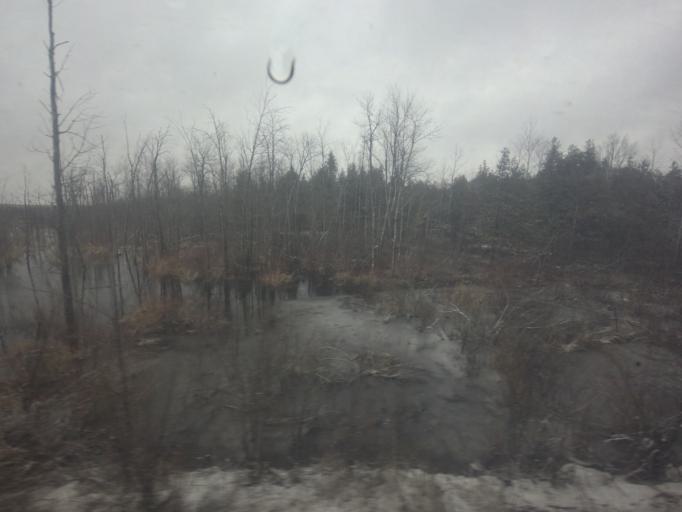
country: CA
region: Ontario
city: Brockville
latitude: 44.7121
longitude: -75.8020
